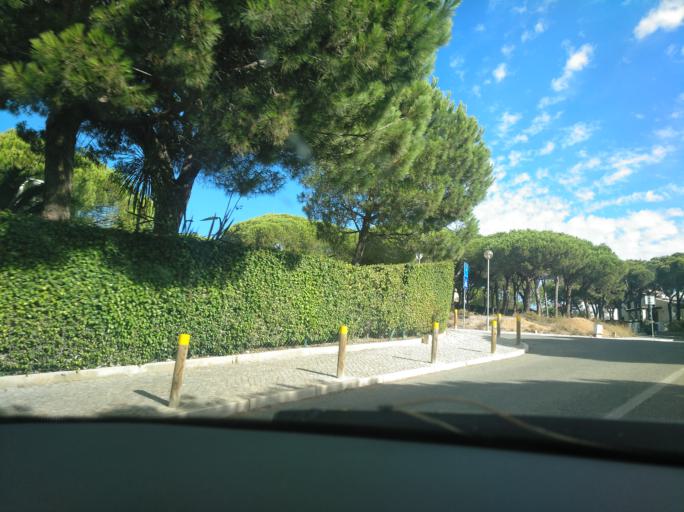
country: PT
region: Faro
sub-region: Vila Real de Santo Antonio
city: Monte Gordo
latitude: 37.1785
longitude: -7.4808
